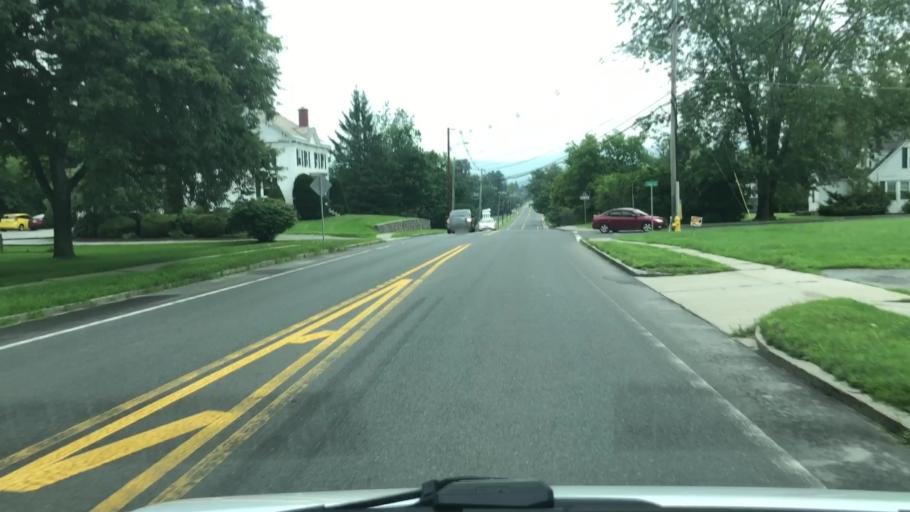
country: US
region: Massachusetts
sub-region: Berkshire County
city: Williamstown
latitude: 42.7016
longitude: -73.1824
